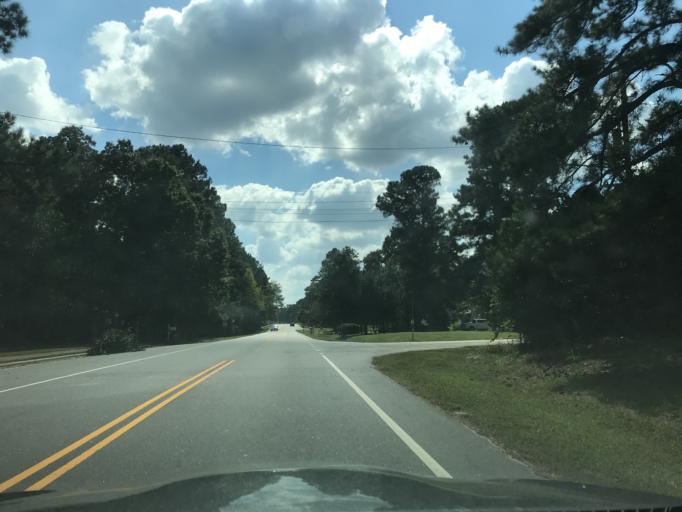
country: US
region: North Carolina
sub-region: Wake County
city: Wake Forest
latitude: 35.9456
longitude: -78.5299
